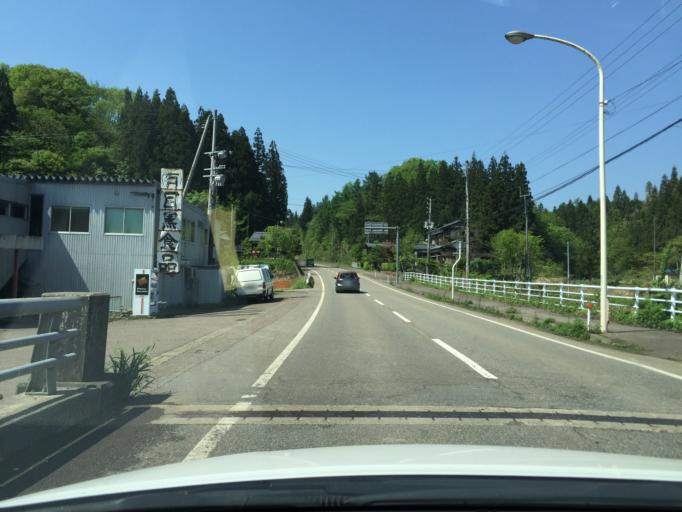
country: JP
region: Niigata
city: Kamo
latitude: 37.6082
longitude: 139.1046
